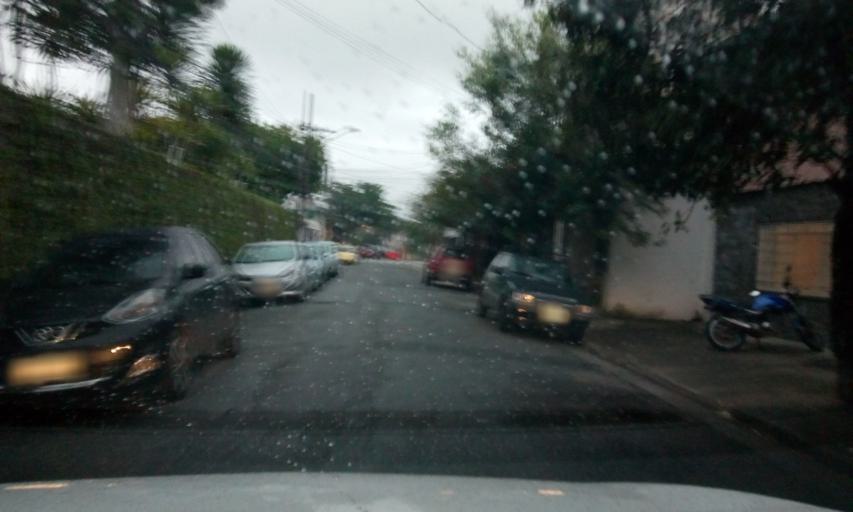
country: BR
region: Sao Paulo
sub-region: Sao Paulo
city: Sao Paulo
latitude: -23.6085
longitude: -46.6903
